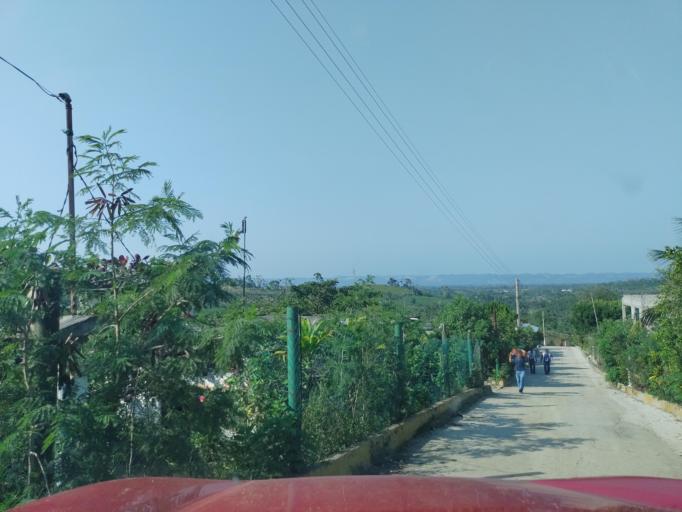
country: MX
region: Veracruz
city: Agua Dulce
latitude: 20.3676
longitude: -97.1858
